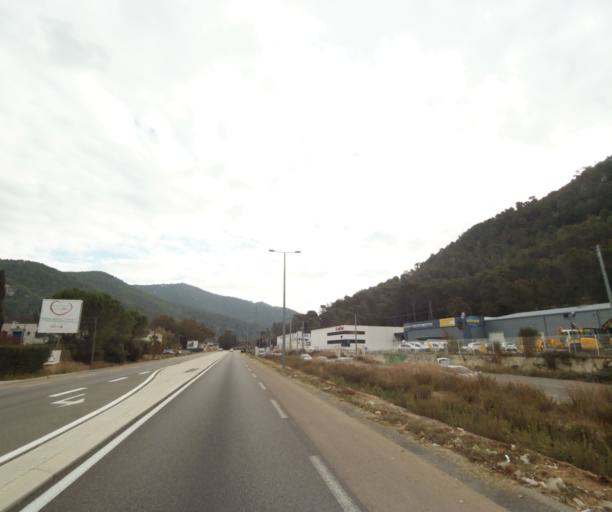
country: FR
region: Provence-Alpes-Cote d'Azur
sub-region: Departement des Bouches-du-Rhone
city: Gemenos
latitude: 43.2770
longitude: 5.6256
